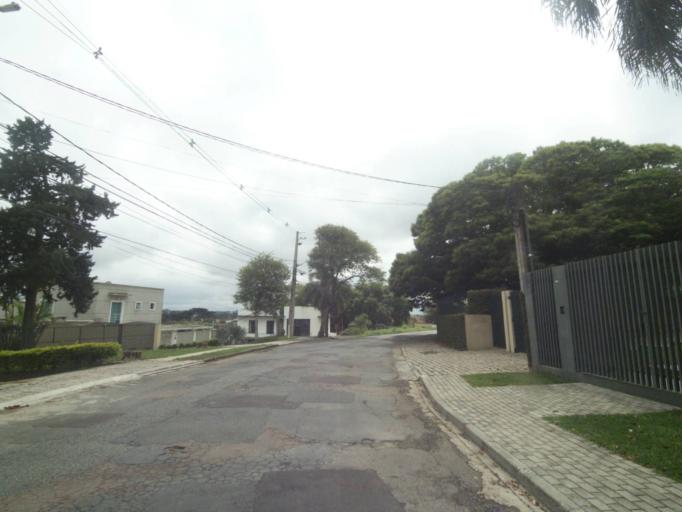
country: BR
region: Parana
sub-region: Curitiba
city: Curitiba
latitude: -25.3931
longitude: -49.2801
